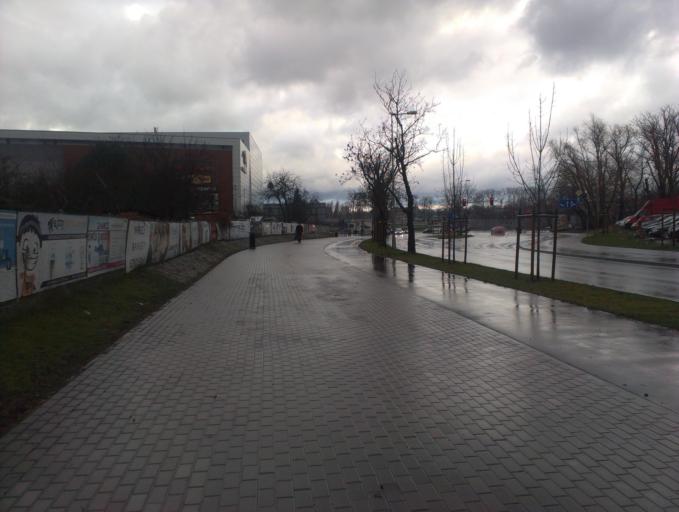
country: PL
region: Greater Poland Voivodeship
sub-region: Poznan
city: Poznan
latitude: 52.4003
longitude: 16.9622
